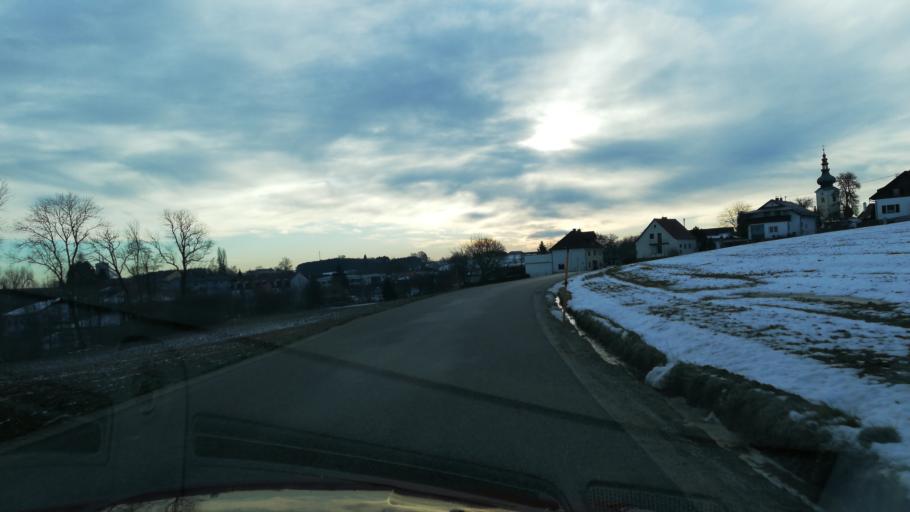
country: AT
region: Upper Austria
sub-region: Wels-Land
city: Buchkirchen
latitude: 48.2261
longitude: 14.0171
